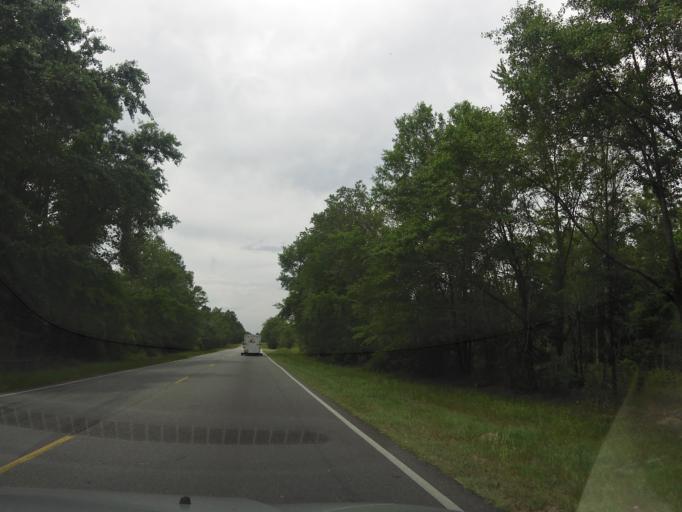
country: US
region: Georgia
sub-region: Candler County
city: Metter
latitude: 32.3863
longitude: -82.1733
